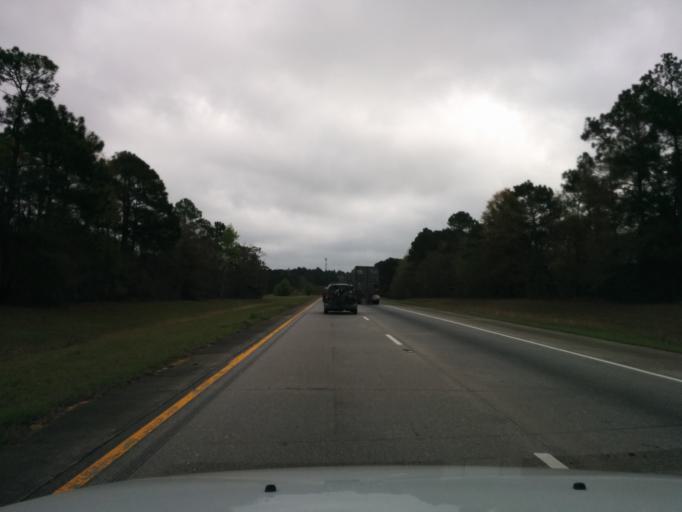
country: US
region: Georgia
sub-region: Candler County
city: Metter
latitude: 32.3822
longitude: -82.2288
